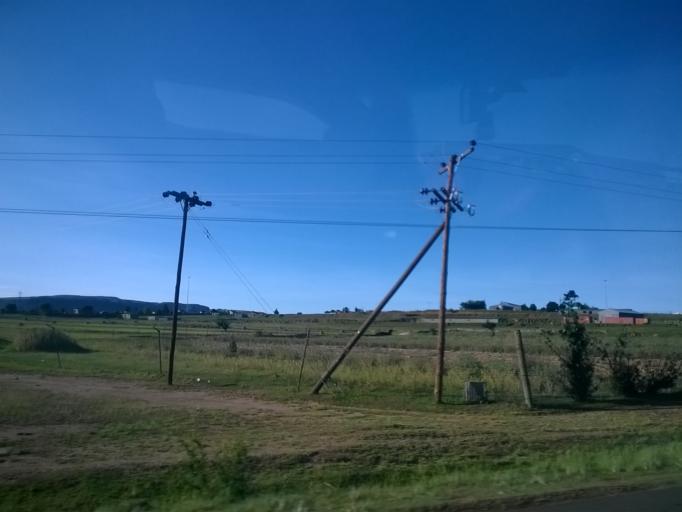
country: LS
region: Maseru
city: Maseru
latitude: -29.2653
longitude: 27.5463
